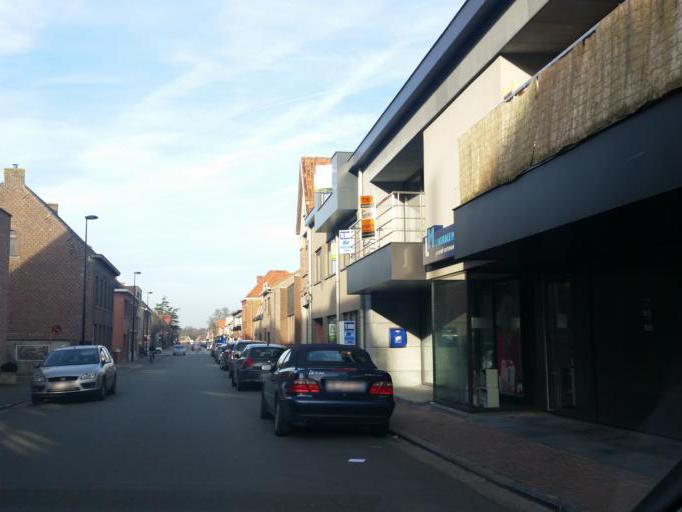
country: BE
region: Flanders
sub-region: Provincie Oost-Vlaanderen
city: Knesselare
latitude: 51.1400
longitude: 3.4117
